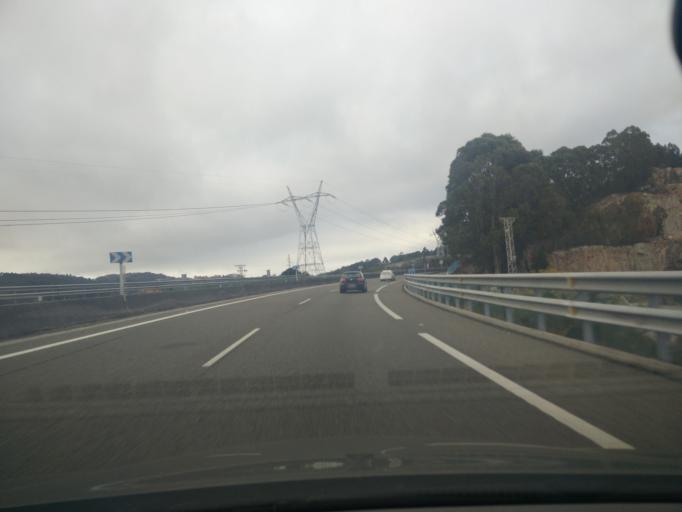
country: ES
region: Galicia
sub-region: Provincia da Coruna
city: Arteixo
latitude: 43.3121
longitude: -8.4757
